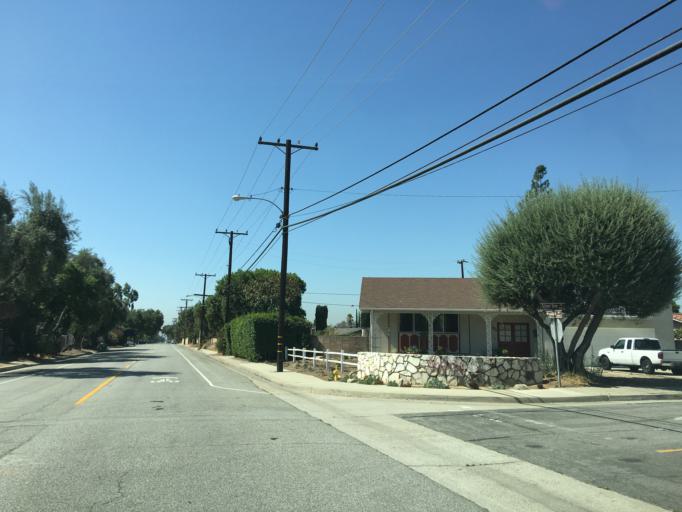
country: US
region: California
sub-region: Los Angeles County
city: Claremont
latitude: 34.1268
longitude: -117.7290
